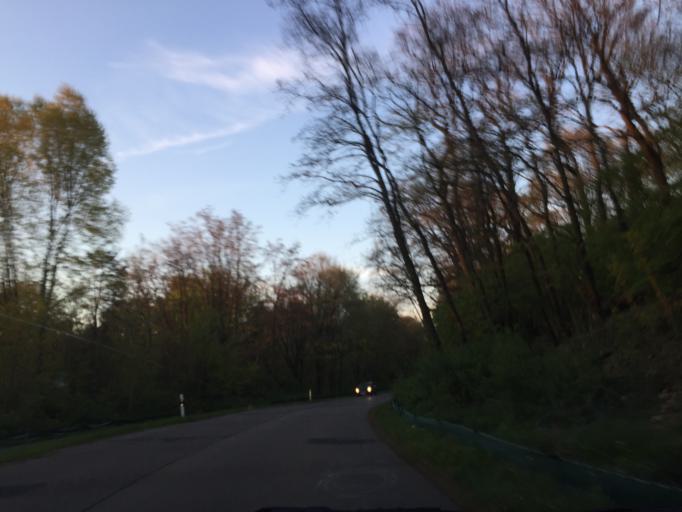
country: DE
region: Brandenburg
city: Potsdam
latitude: 52.3798
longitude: 13.0404
